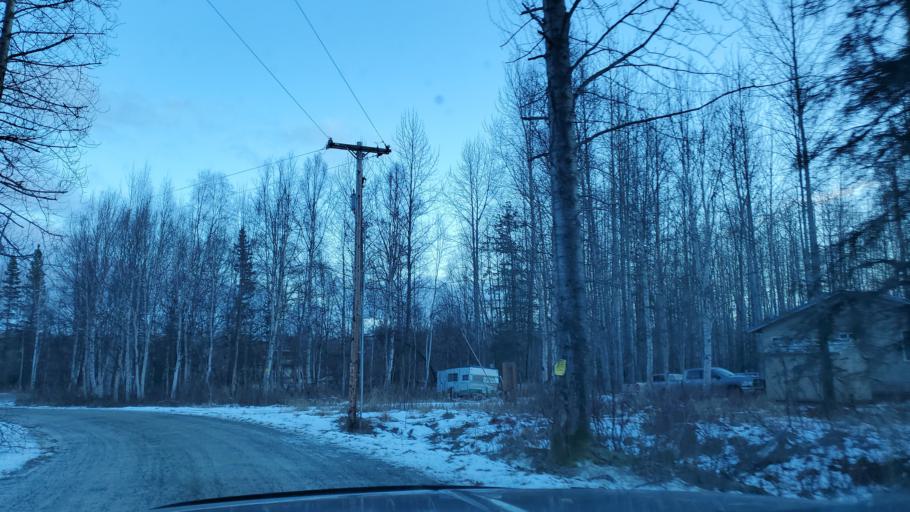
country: US
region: Alaska
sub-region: Matanuska-Susitna Borough
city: Lakes
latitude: 61.6652
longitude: -149.3380
